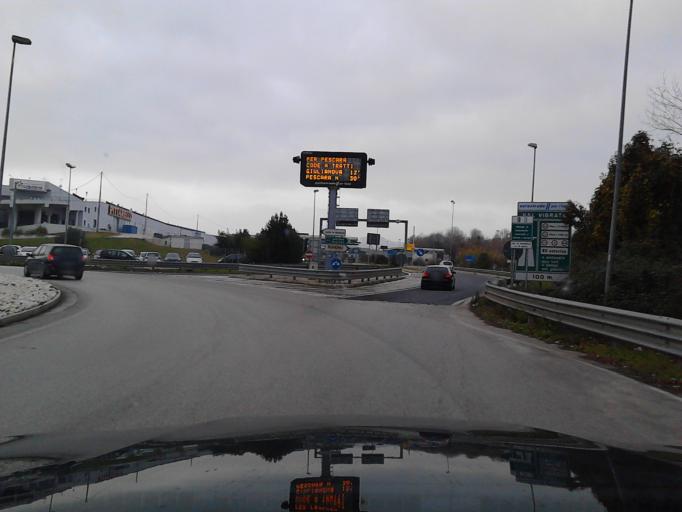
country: IT
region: Abruzzo
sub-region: Provincia di Teramo
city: Alba Adriatica
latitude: 42.8338
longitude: 13.9035
